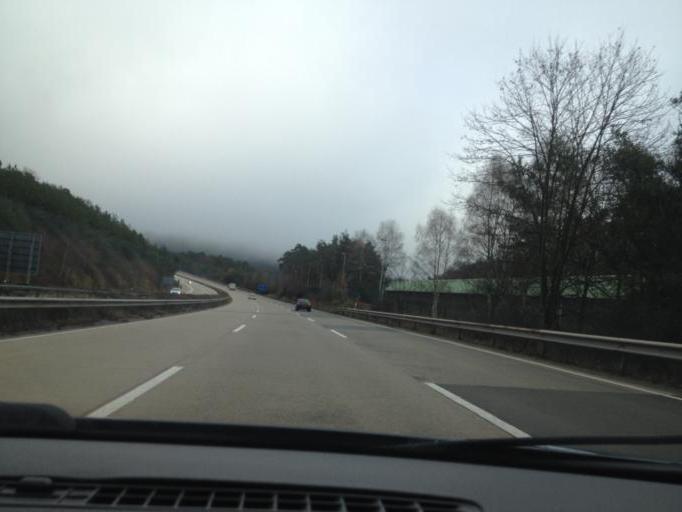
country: DE
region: Rheinland-Pfalz
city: Mehlingen
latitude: 49.4523
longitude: 7.8257
